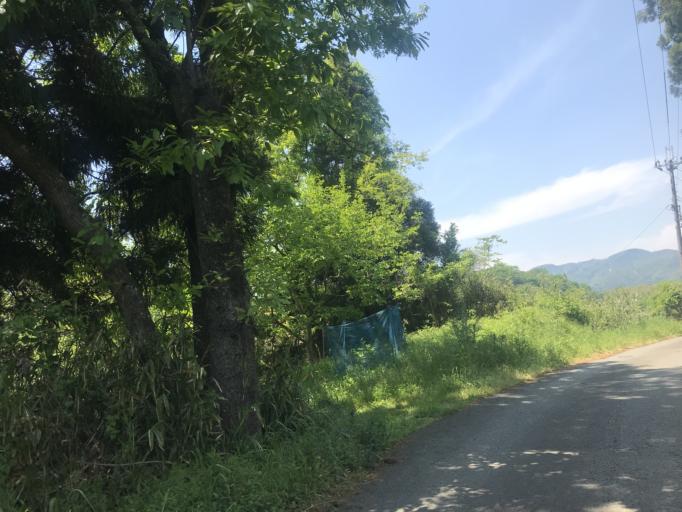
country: JP
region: Kyoto
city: Kameoka
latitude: 35.0692
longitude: 135.5702
